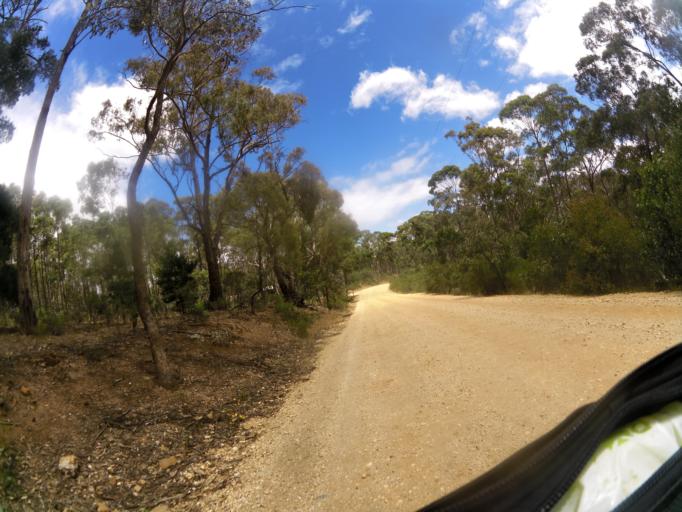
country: AU
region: Victoria
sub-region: Mount Alexander
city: Castlemaine
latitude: -37.0316
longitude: 144.2534
